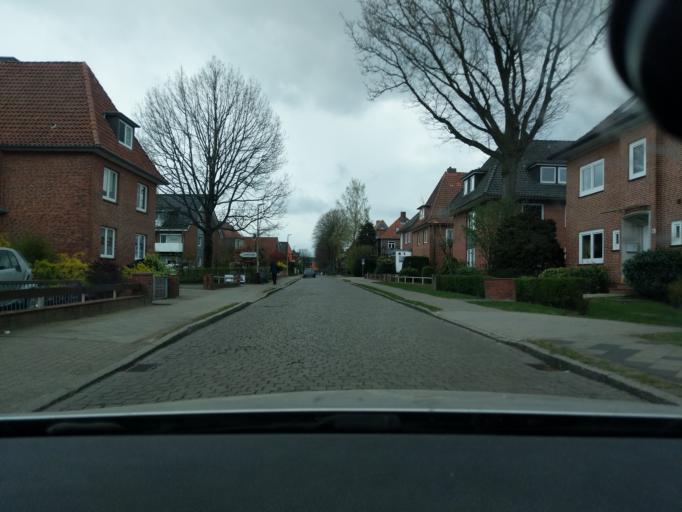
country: DE
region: Lower Saxony
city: Stade
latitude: 53.5909
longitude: 9.4666
